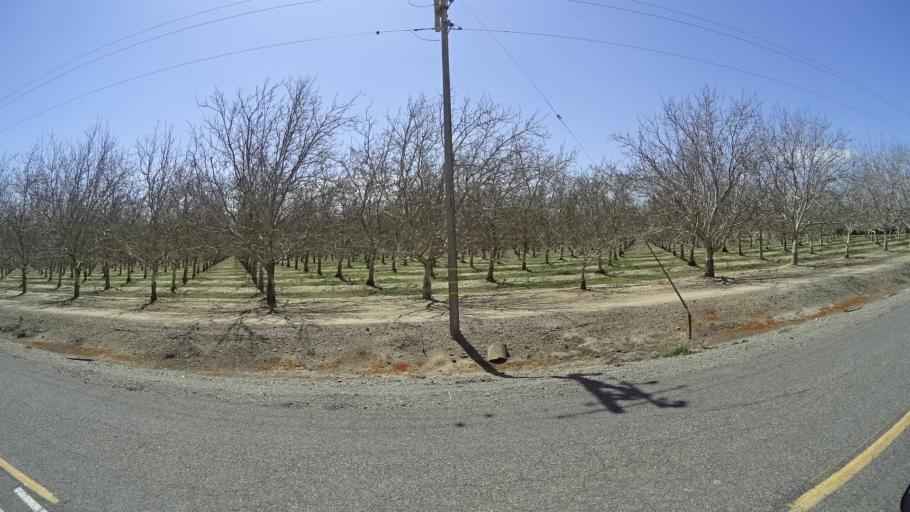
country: US
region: California
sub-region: Glenn County
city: Hamilton City
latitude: 39.6525
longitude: -122.1016
